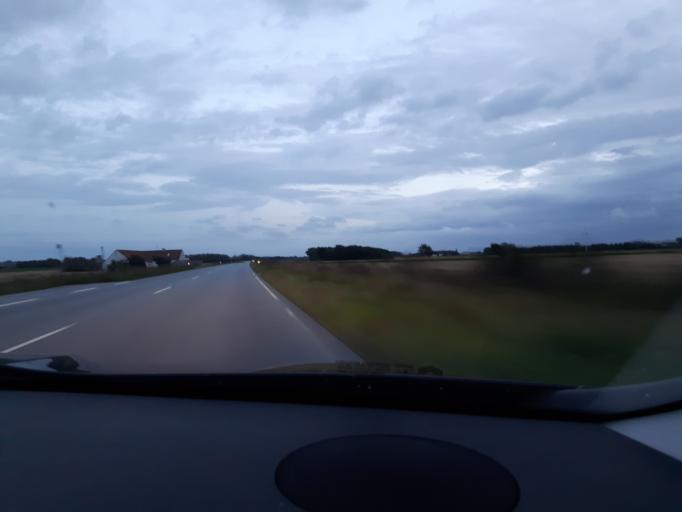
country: DK
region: North Denmark
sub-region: Hjorring Kommune
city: Hjorring
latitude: 57.4926
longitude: 9.9450
